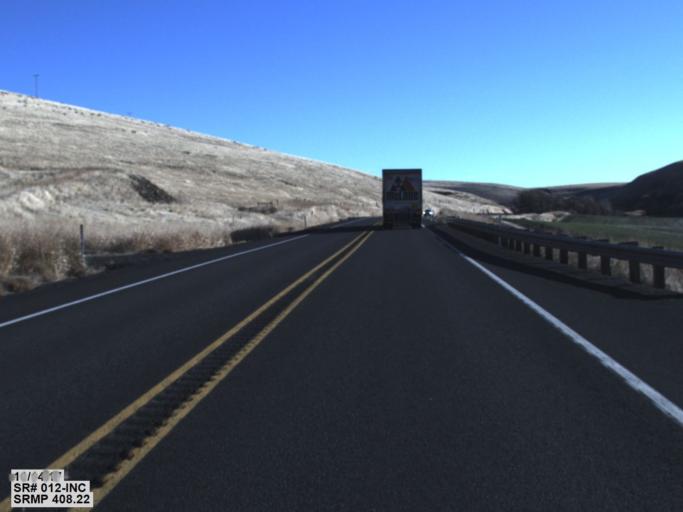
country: US
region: Washington
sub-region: Garfield County
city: Pomeroy
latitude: 46.4677
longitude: -117.5024
